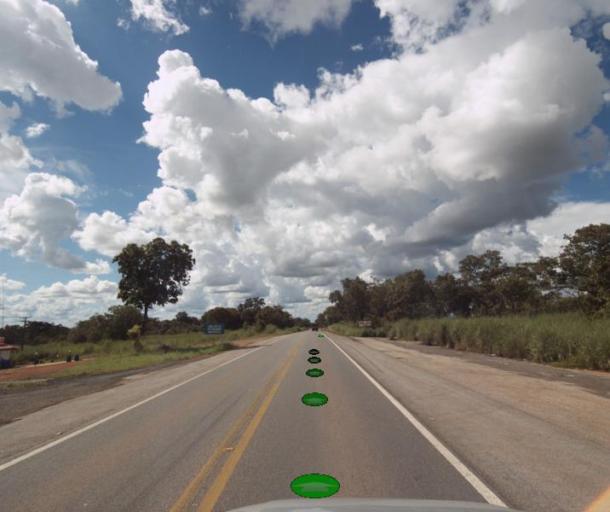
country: BR
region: Goias
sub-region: Porangatu
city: Porangatu
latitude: -13.3881
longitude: -49.1285
